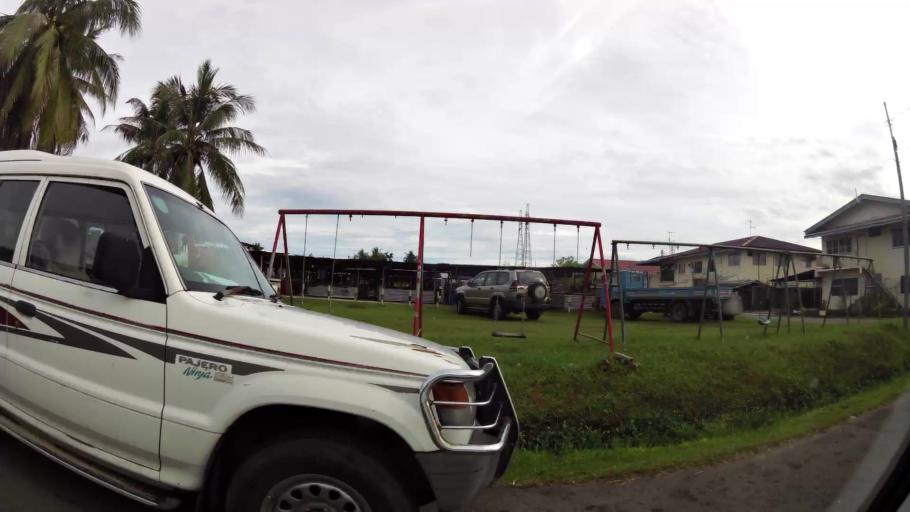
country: BN
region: Belait
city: Seria
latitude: 4.6160
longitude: 114.3491
